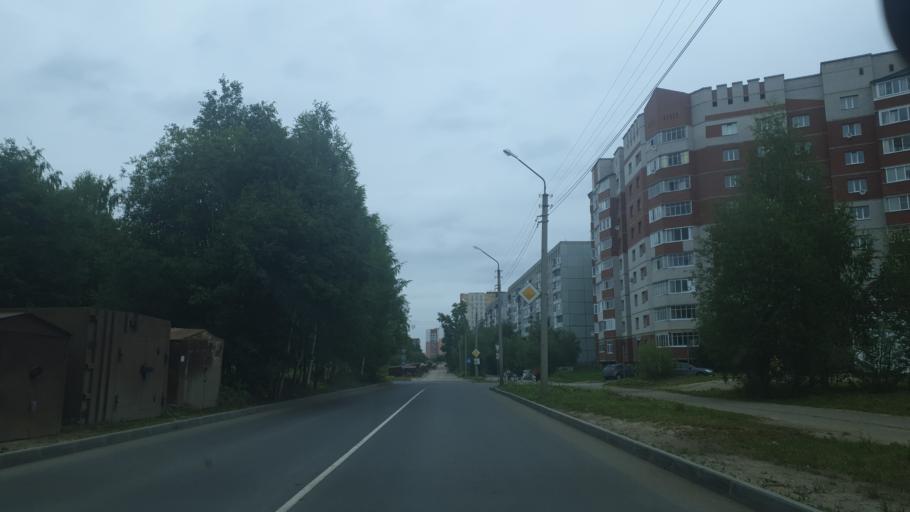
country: RU
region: Komi Republic
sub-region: Syktyvdinskiy Rayon
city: Syktyvkar
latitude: 61.6955
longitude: 50.8069
